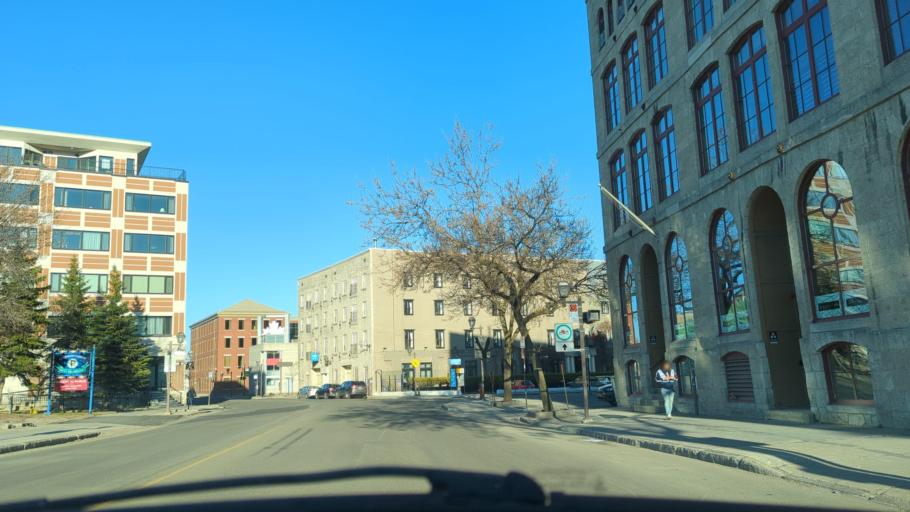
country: CA
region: Quebec
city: Quebec
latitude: 46.8168
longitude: -71.2043
